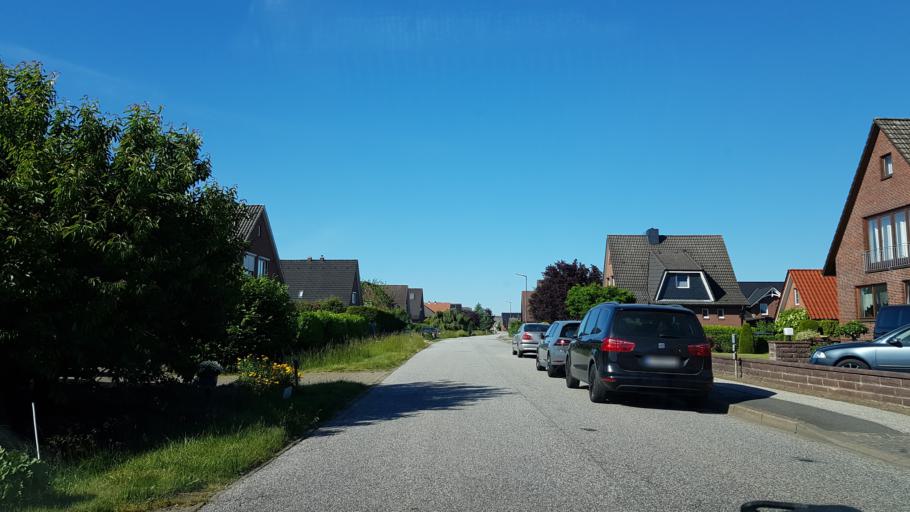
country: DE
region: Lower Saxony
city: Neu Wulmstorf
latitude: 53.5164
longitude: 9.7968
